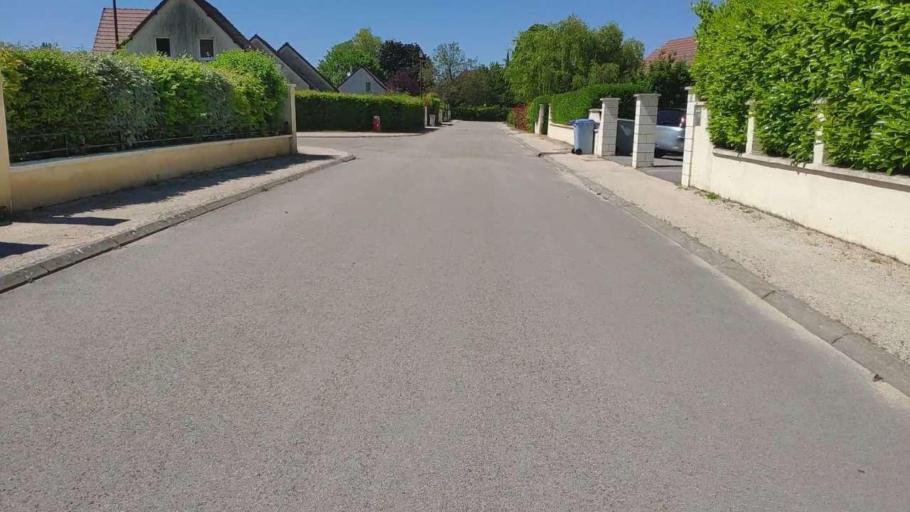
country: FR
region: Franche-Comte
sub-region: Departement du Jura
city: Perrigny
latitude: 46.7506
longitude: 5.6164
